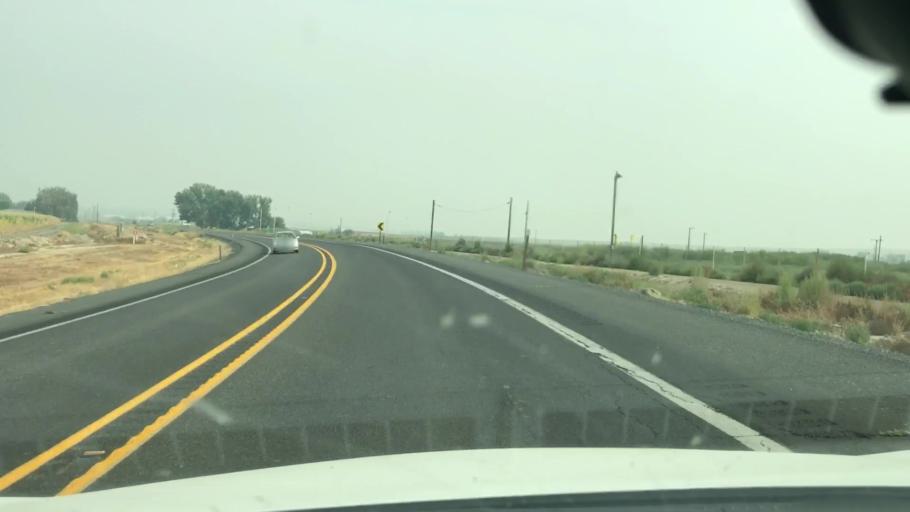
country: US
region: Washington
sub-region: Grant County
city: Quincy
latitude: 47.2348
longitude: -119.7461
